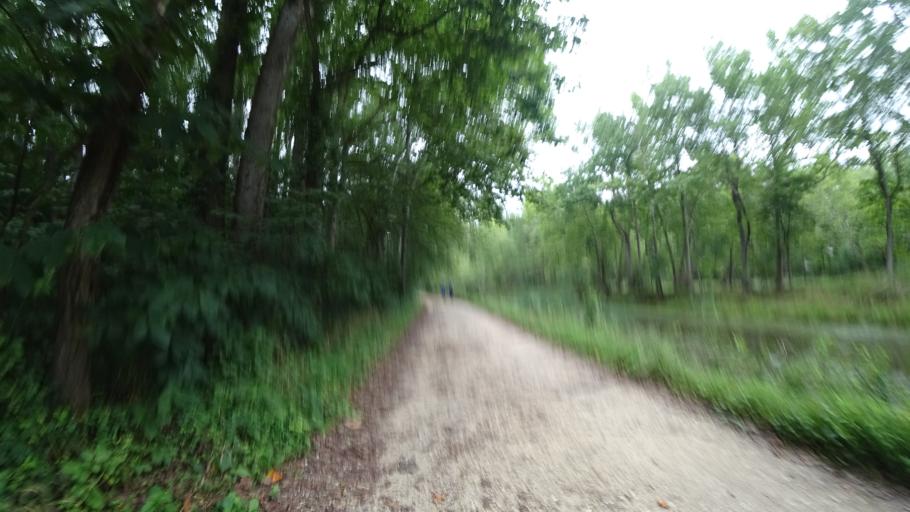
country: US
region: Maryland
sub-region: Montgomery County
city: Potomac
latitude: 38.9790
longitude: -77.2242
